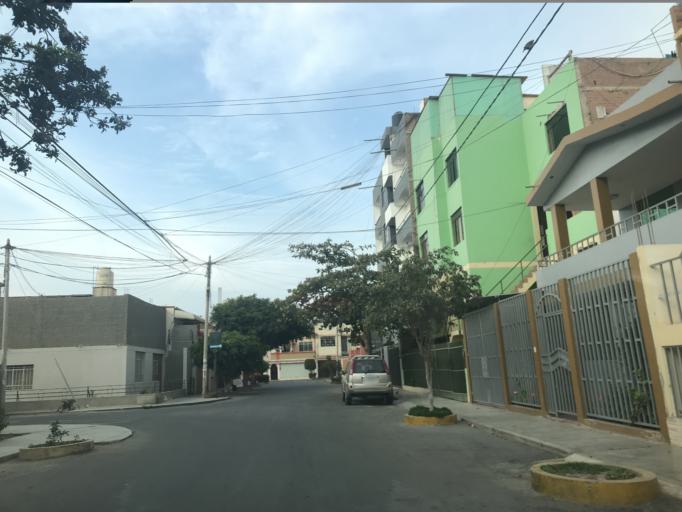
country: PE
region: Lambayeque
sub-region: Provincia de Chiclayo
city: Chiclayo
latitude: -6.7857
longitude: -79.8430
